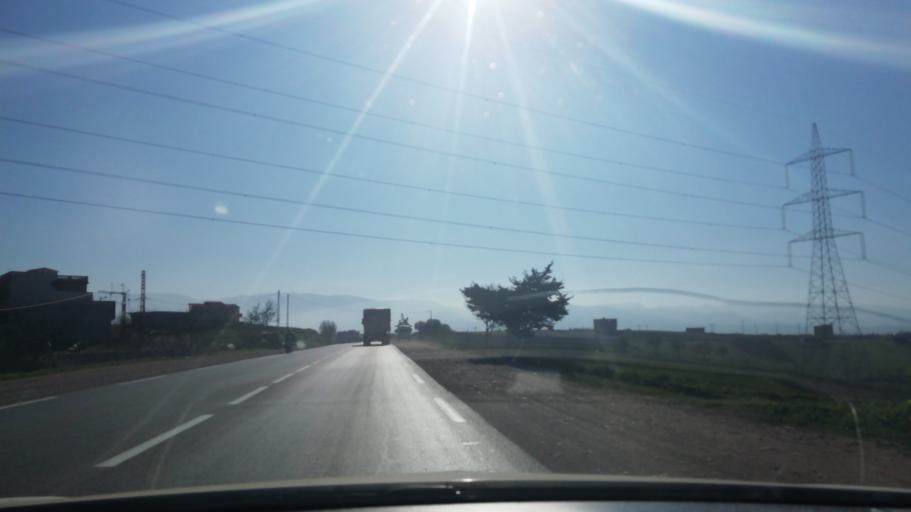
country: DZ
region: Tlemcen
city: Nedroma
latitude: 35.0819
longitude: -1.7922
